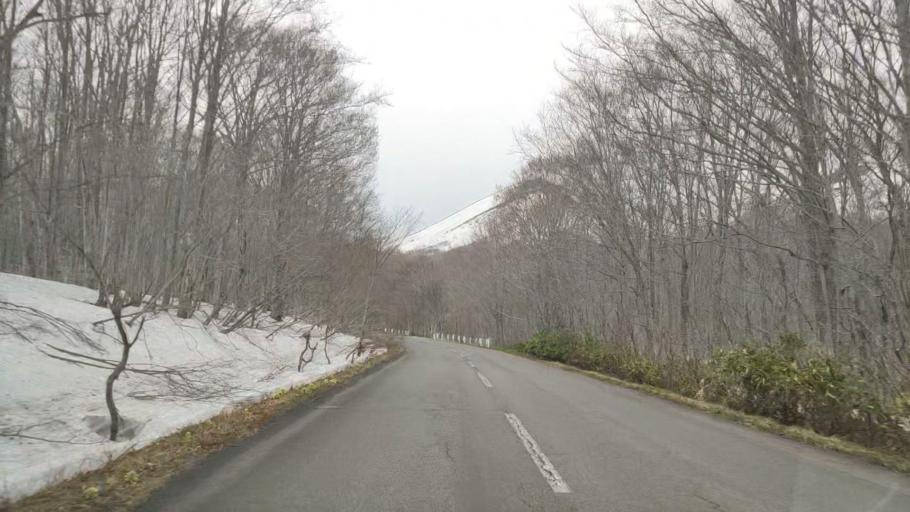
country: JP
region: Aomori
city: Aomori Shi
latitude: 40.6532
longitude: 140.9487
